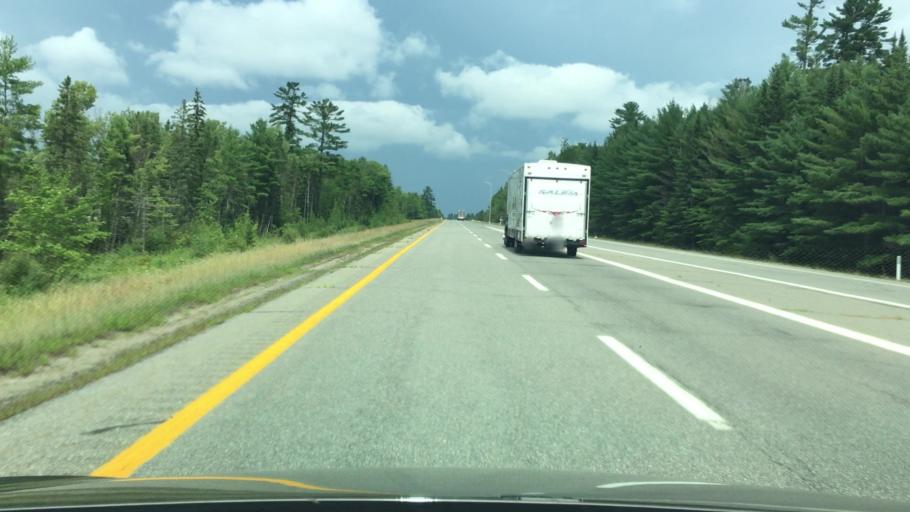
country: US
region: Maine
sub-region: Penobscot County
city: Lincoln
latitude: 45.3784
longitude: -68.6046
